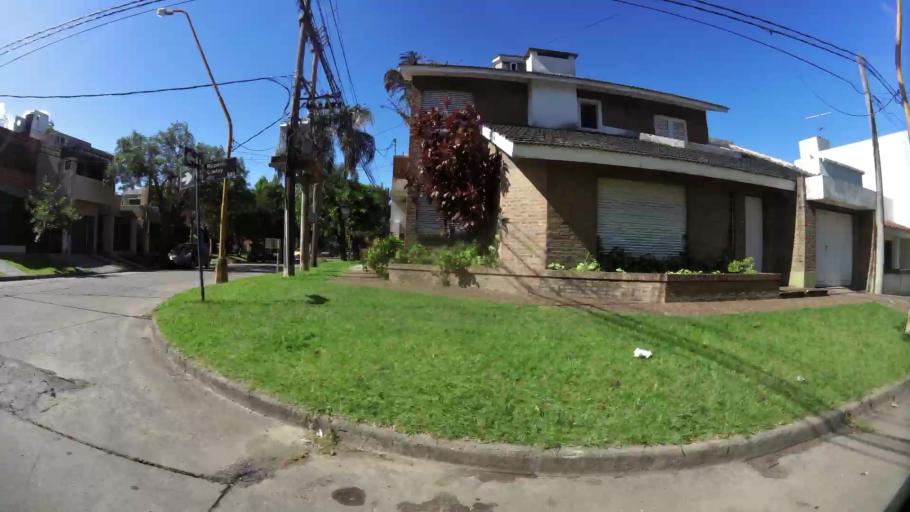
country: AR
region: Santa Fe
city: Santa Fe de la Vera Cruz
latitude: -31.6195
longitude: -60.6787
